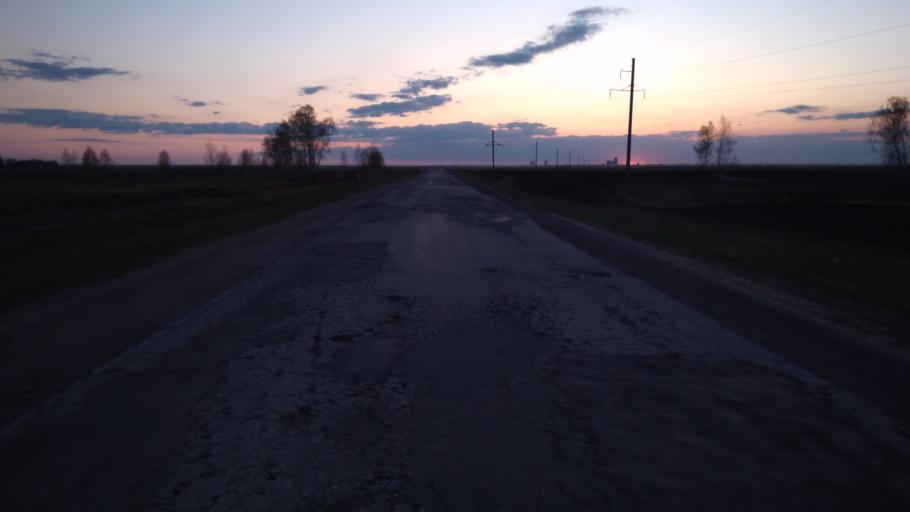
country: RU
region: Chelyabinsk
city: Bobrovka
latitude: 54.0861
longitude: 61.6665
